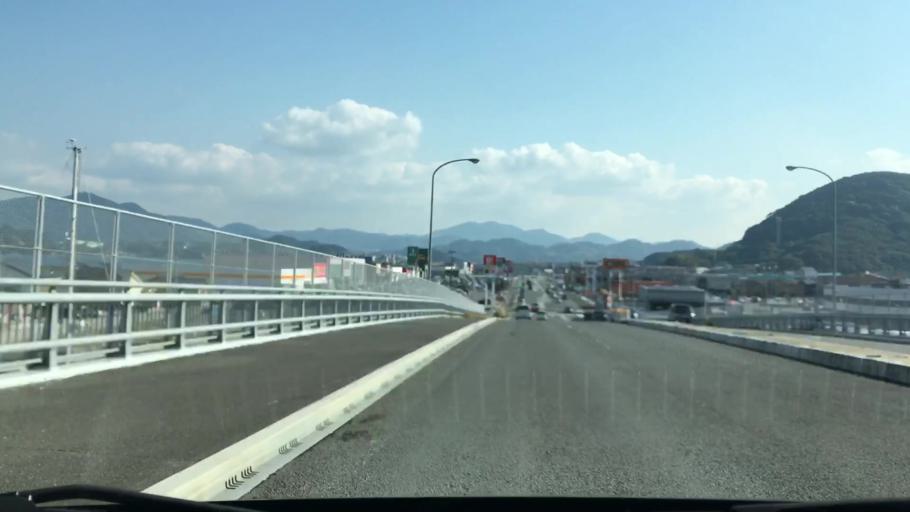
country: JP
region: Nagasaki
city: Togitsu
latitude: 32.8537
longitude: 129.8236
